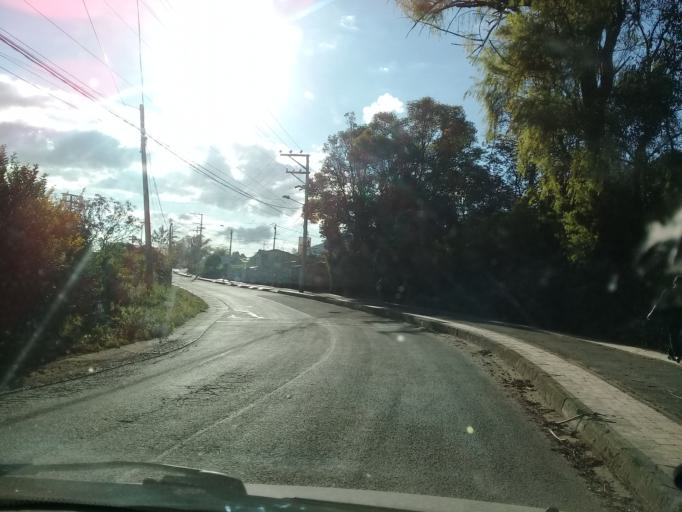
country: CO
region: Cundinamarca
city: Tenjo
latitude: 4.8771
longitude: -74.1374
